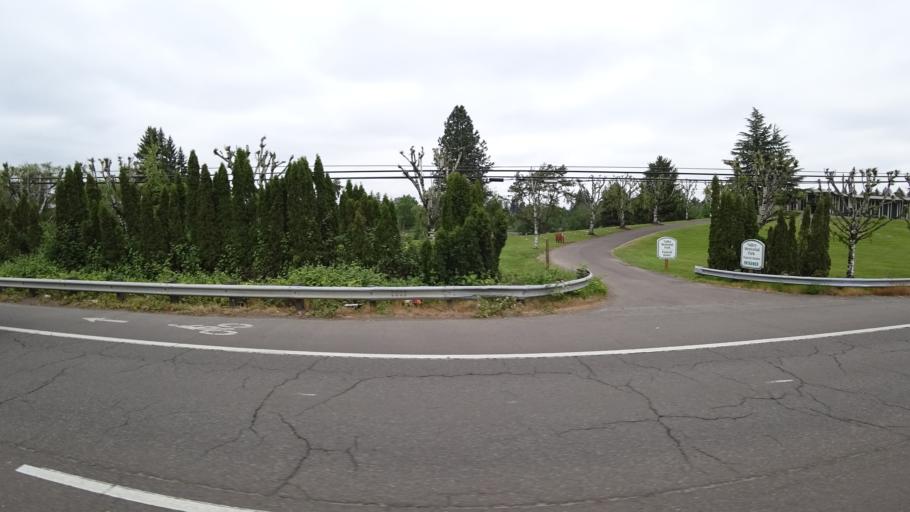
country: US
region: Oregon
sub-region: Washington County
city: Hillsboro
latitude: 45.5019
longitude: -122.9448
